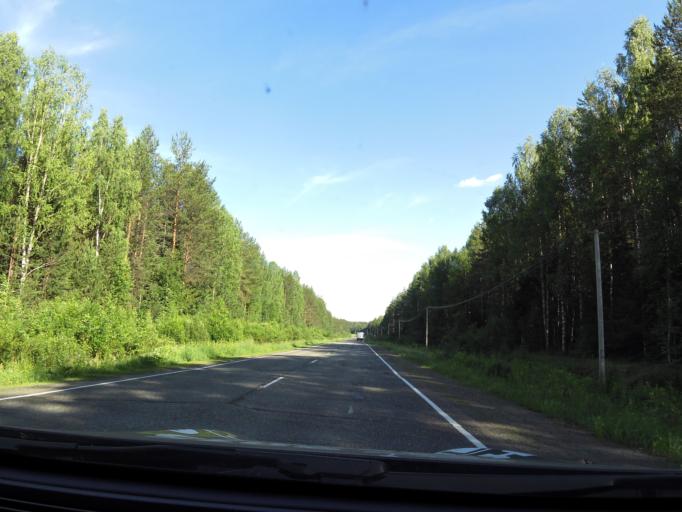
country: RU
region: Kirov
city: Dubrovka
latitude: 58.9093
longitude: 51.1769
